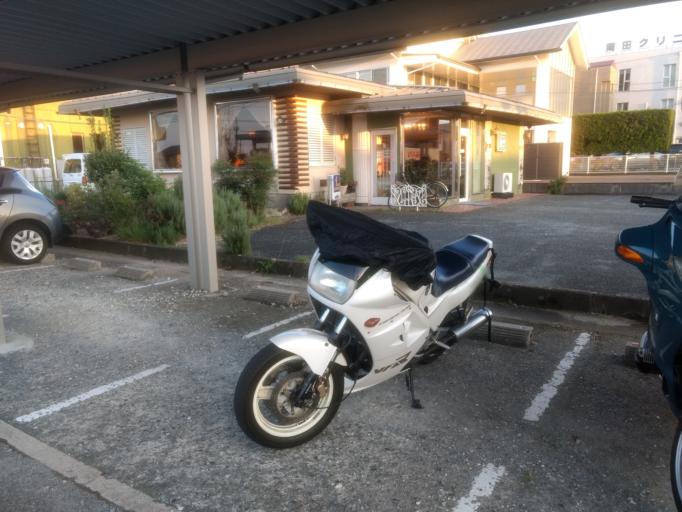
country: JP
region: Yamaguchi
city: Nagato
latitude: 34.3682
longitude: 131.1823
